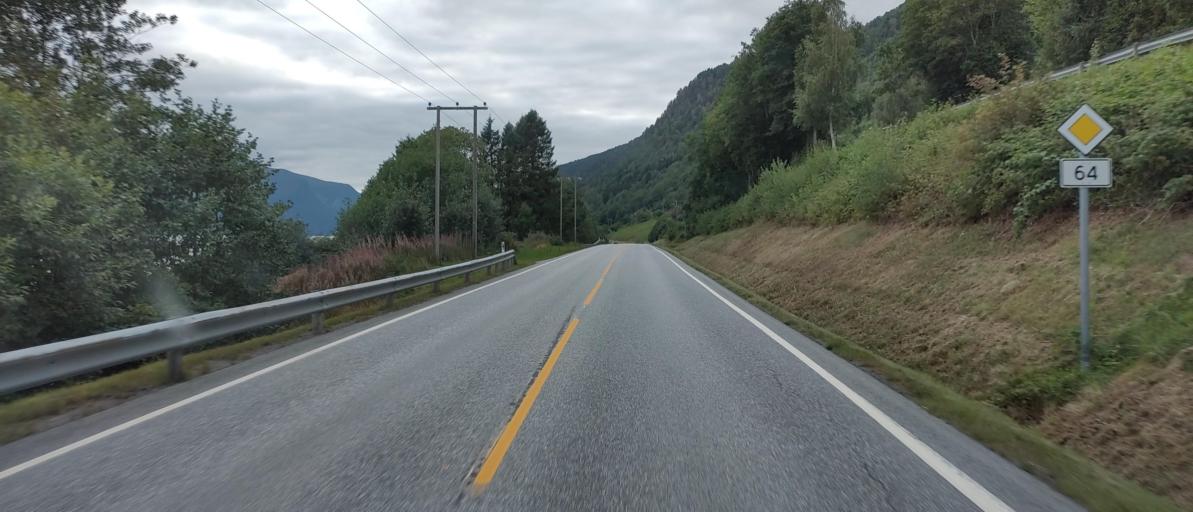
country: NO
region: More og Romsdal
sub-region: Rauma
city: Andalsnes
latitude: 62.5814
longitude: 7.6975
